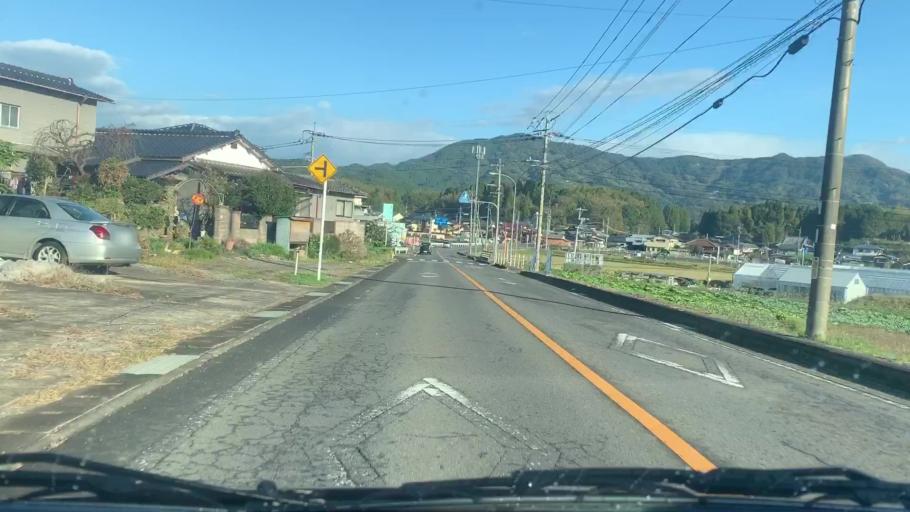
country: JP
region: Saga Prefecture
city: Takeocho-takeo
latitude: 33.2188
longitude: 130.0281
